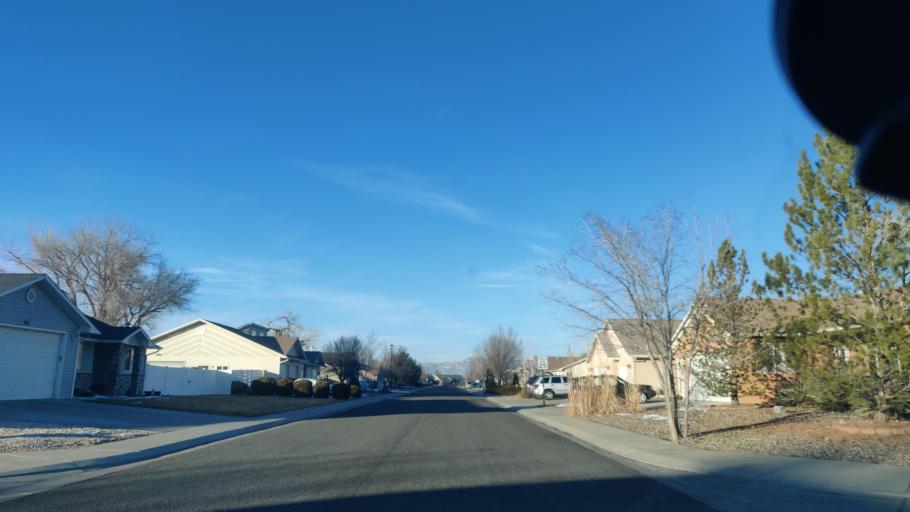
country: US
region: Colorado
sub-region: Mesa County
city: Grand Junction
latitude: 39.0589
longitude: -108.5241
